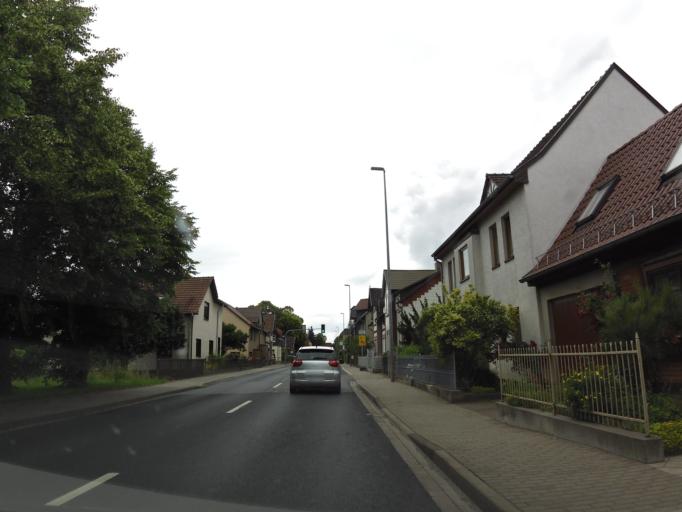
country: DE
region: Thuringia
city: Leimbach
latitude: 50.8146
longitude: 10.2001
